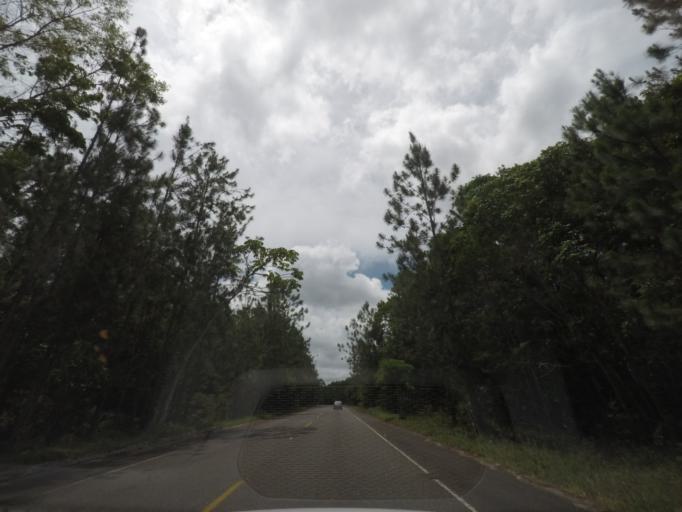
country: BR
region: Bahia
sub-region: Conde
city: Conde
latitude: -12.1006
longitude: -37.7791
